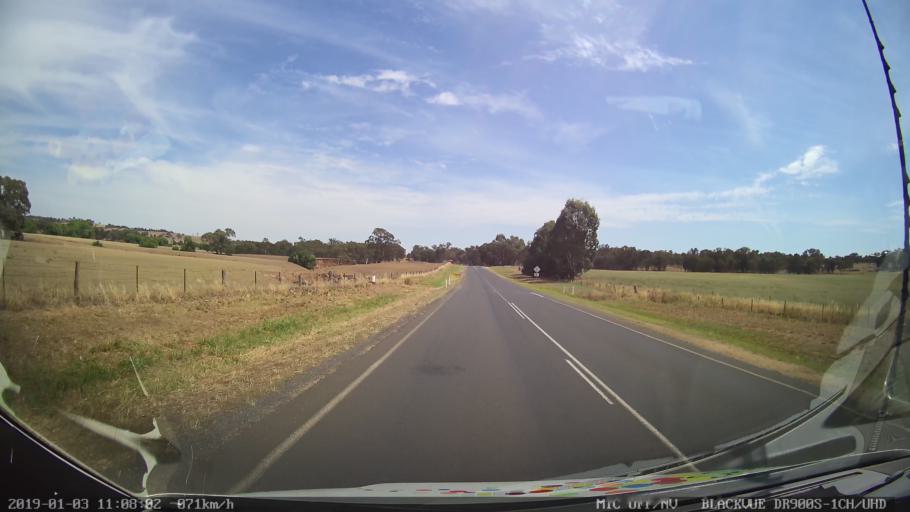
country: AU
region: New South Wales
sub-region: Young
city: Young
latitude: -34.2537
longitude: 148.2586
